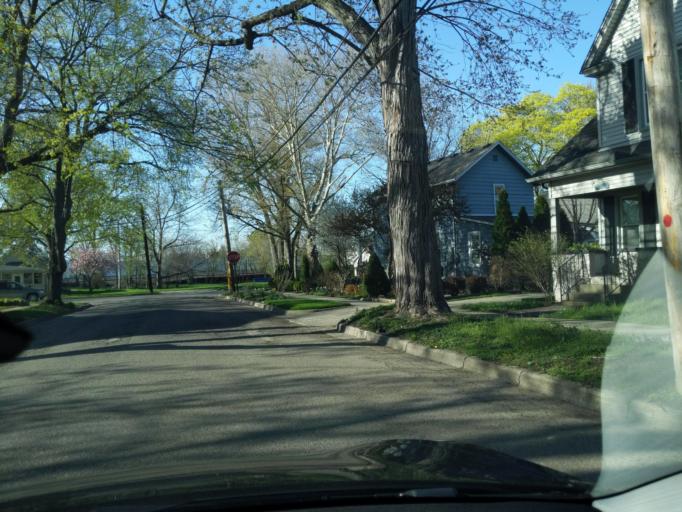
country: US
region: Michigan
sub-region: Washtenaw County
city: Chelsea
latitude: 42.3165
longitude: -84.0247
